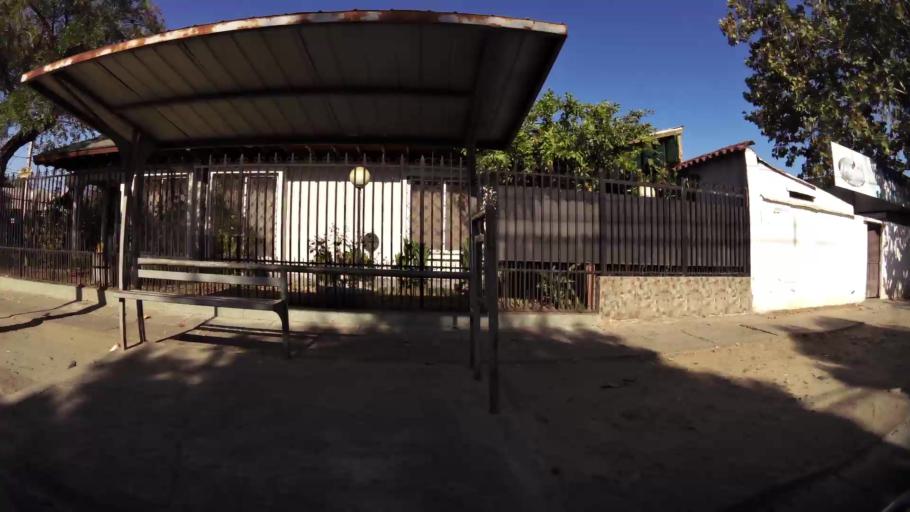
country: CL
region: Maule
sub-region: Provincia de Talca
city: Talca
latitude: -35.4407
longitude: -71.6666
